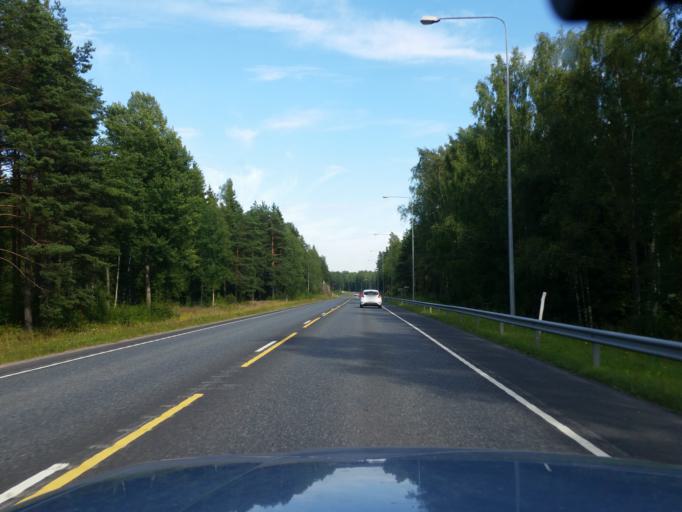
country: FI
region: Uusimaa
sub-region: Helsinki
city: Siuntio
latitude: 60.0988
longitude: 24.3108
